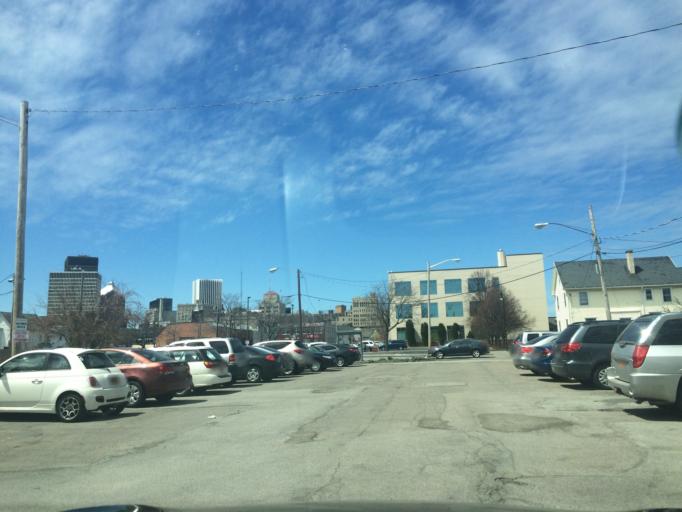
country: US
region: New York
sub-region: Monroe County
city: Rochester
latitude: 43.1566
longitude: -77.5936
